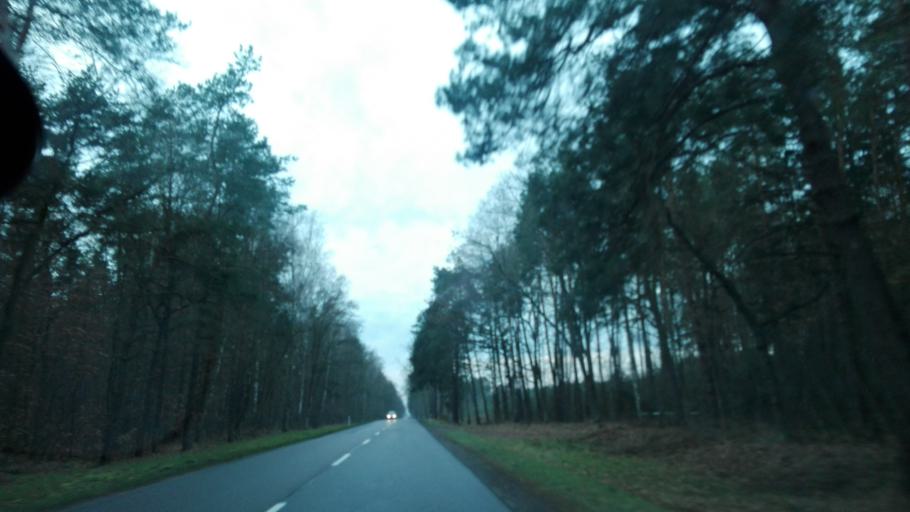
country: PL
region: Lublin Voivodeship
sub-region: Powiat radzynski
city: Radzyn Podlaski
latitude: 51.7784
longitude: 22.6838
